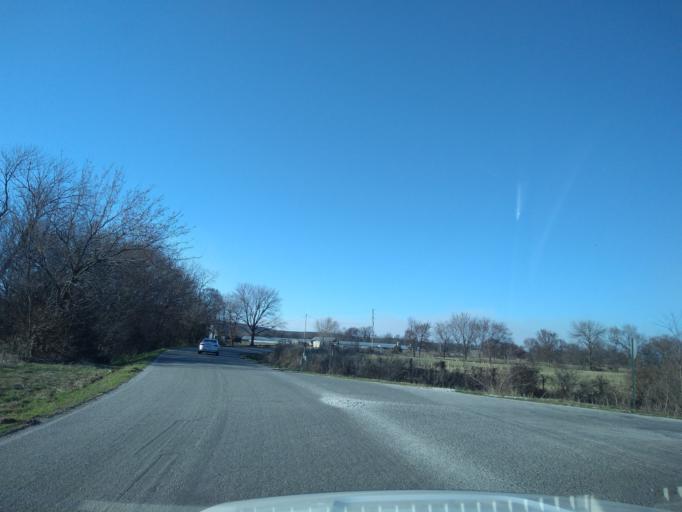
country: US
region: Arkansas
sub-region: Washington County
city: Lincoln
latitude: 36.0160
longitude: -94.3925
